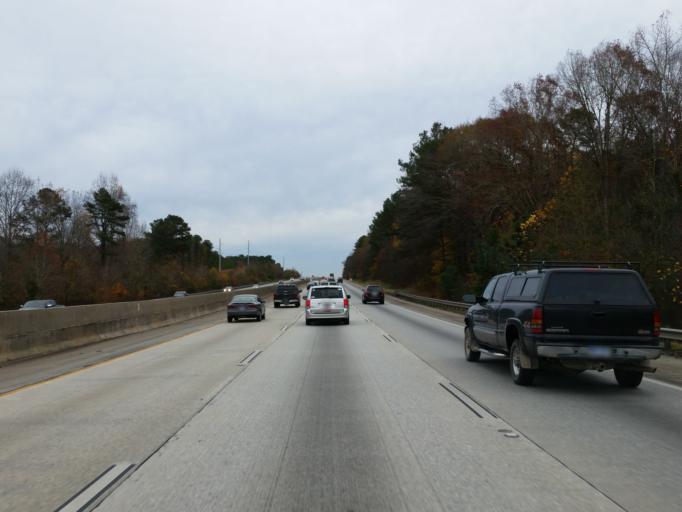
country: US
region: Georgia
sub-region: Monroe County
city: Forsyth
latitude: 33.0082
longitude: -83.8736
